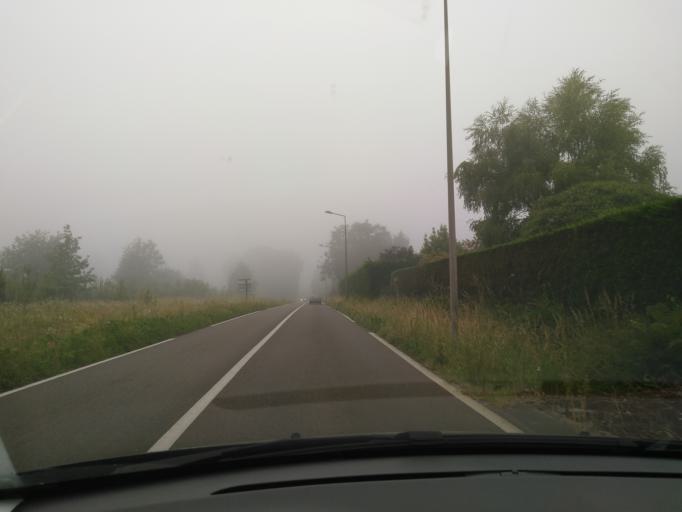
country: FR
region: Aquitaine
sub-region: Departement des Landes
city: Villeneuve-de-Marsan
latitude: 43.8898
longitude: -0.3970
